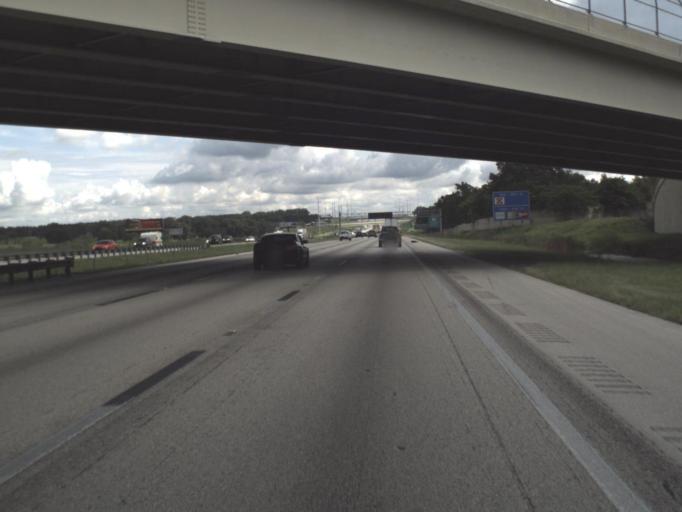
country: US
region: Florida
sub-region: Polk County
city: Winston
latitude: 28.0620
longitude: -82.0011
